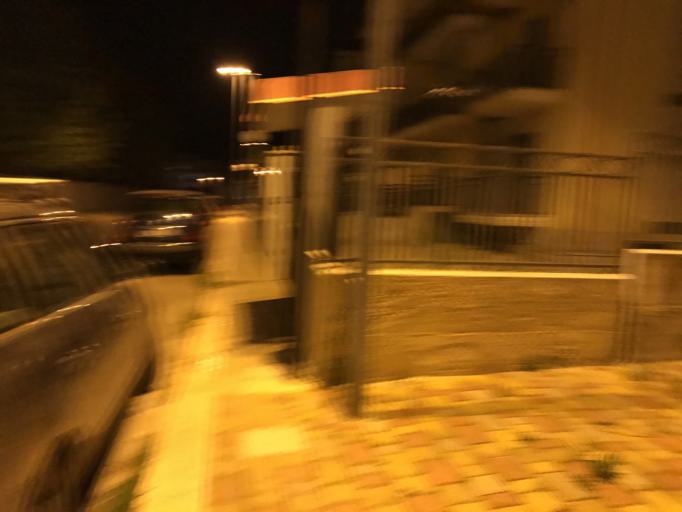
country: IT
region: Apulia
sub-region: Provincia di Bari
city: Corato
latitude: 41.1550
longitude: 16.4017
